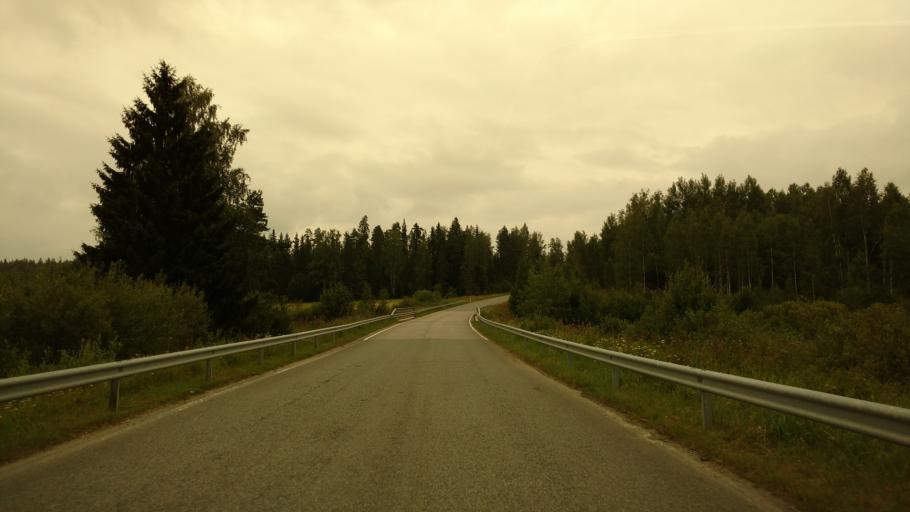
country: FI
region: Haeme
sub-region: Forssa
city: Ypaejae
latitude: 60.7665
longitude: 23.2182
